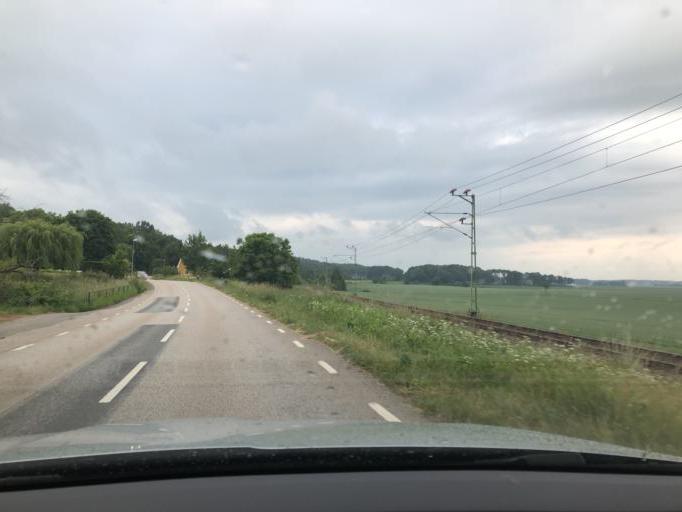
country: SE
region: Blekinge
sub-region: Solvesborgs Kommun
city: Soelvesborg
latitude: 56.1113
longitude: 14.6209
